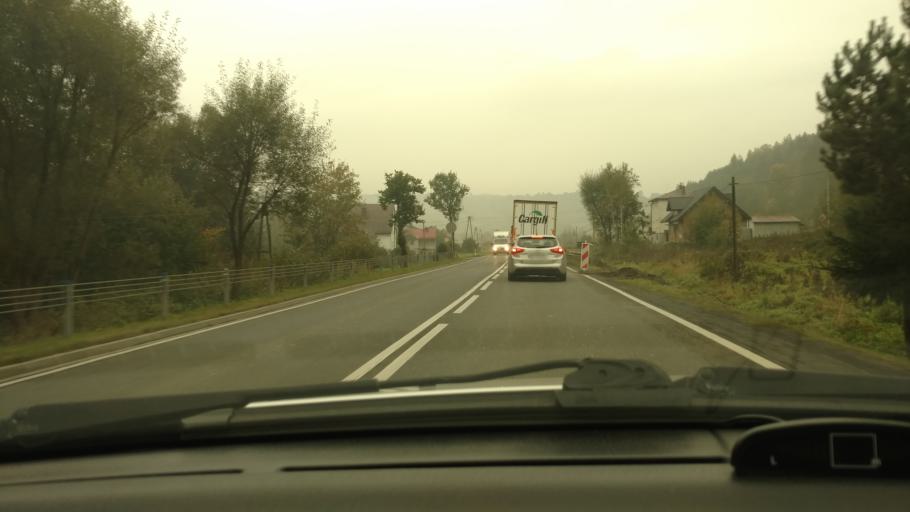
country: PL
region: Lesser Poland Voivodeship
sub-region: Powiat nowosadecki
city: Nawojowa
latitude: 49.6118
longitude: 20.7664
